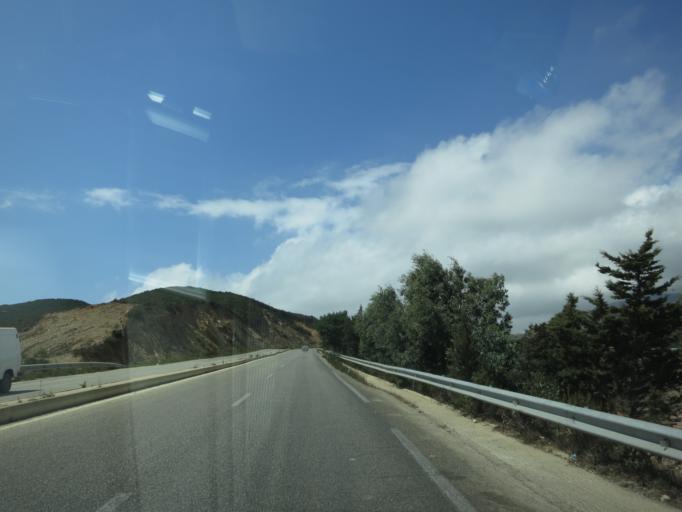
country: ES
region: Ceuta
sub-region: Ceuta
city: Ceuta
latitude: 35.8696
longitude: -5.3696
